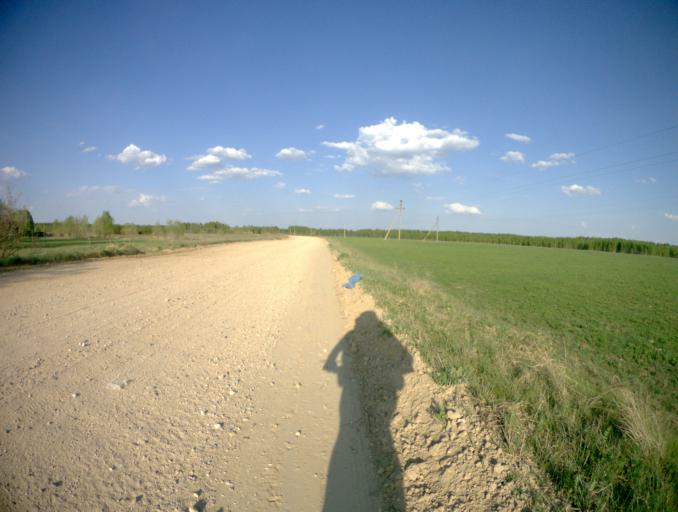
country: RU
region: Vladimir
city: Mstera
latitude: 56.5529
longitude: 41.7233
